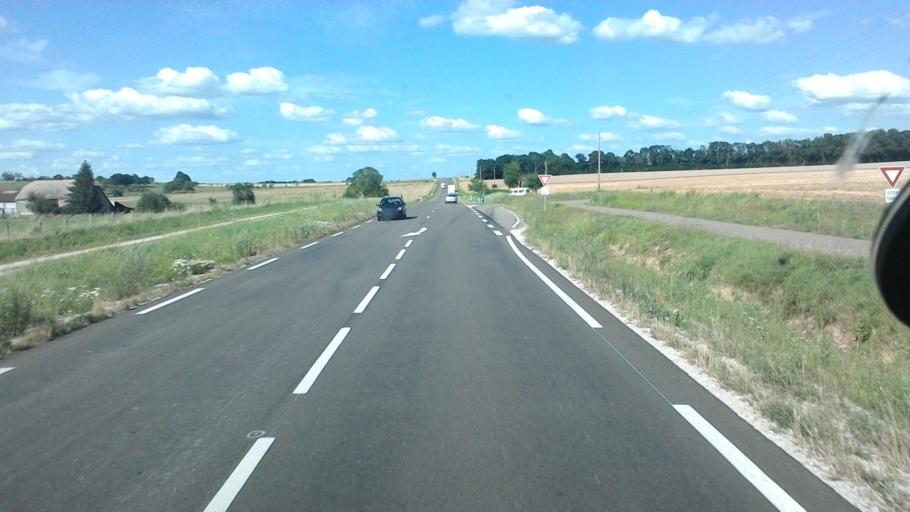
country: FR
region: Franche-Comte
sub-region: Departement de la Haute-Saone
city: Gy
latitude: 47.4560
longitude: 5.9020
